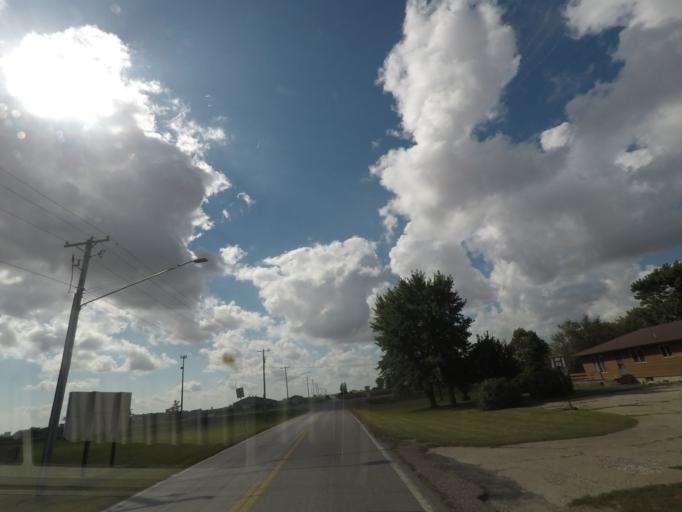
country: US
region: Iowa
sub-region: Story County
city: Nevada
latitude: 42.0094
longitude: -93.3192
